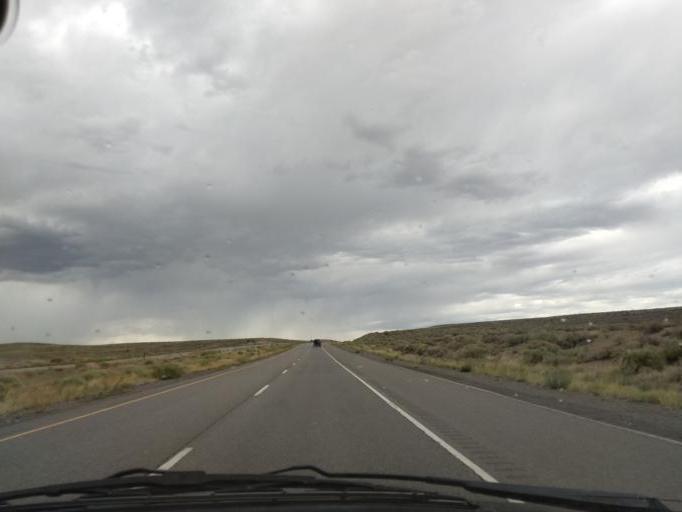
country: US
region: Colorado
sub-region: Delta County
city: Delta
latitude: 38.7675
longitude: -108.2205
